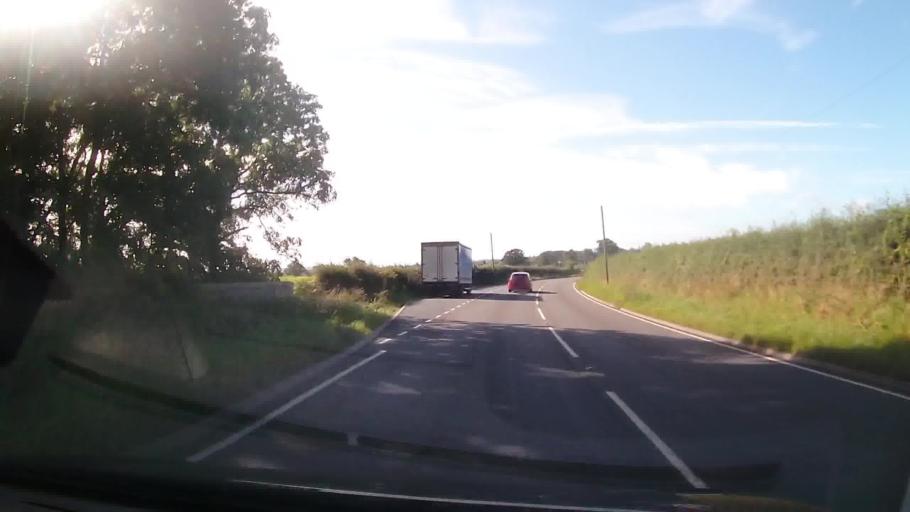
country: GB
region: England
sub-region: Shropshire
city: Clive
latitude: 52.7985
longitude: -2.6998
